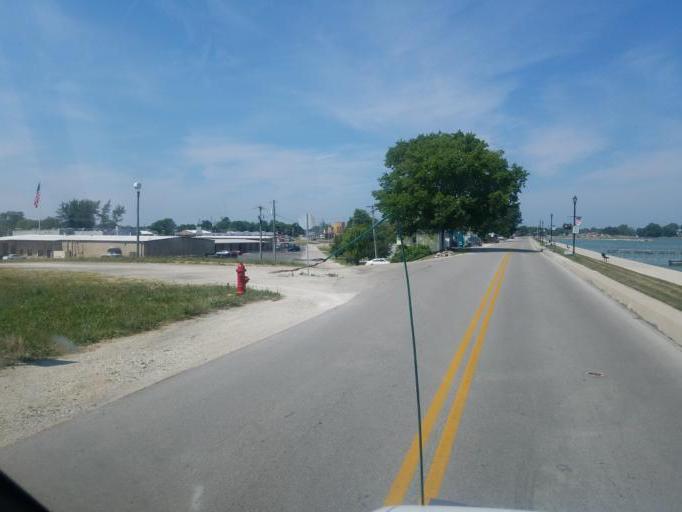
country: US
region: Ohio
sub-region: Mercer County
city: Celina
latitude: 40.5375
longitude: -84.5740
